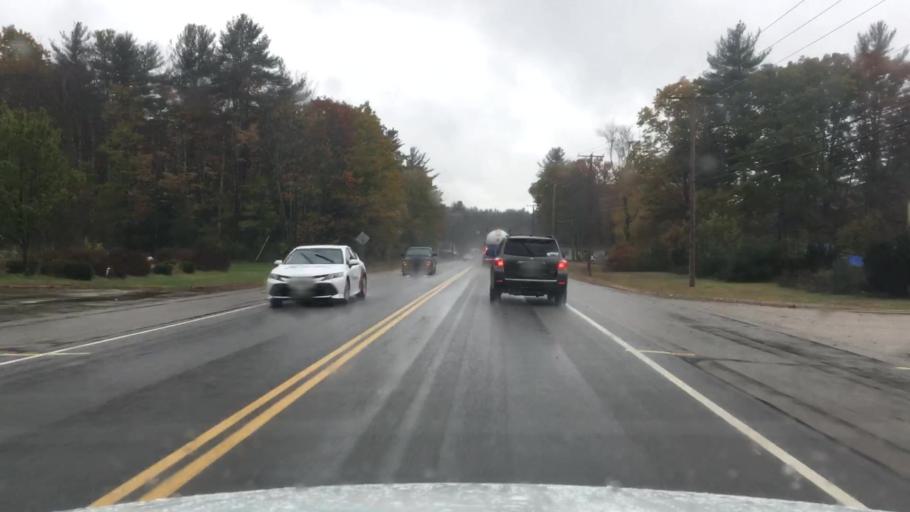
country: US
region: New Hampshire
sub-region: Strafford County
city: Rochester
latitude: 43.2518
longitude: -70.9801
